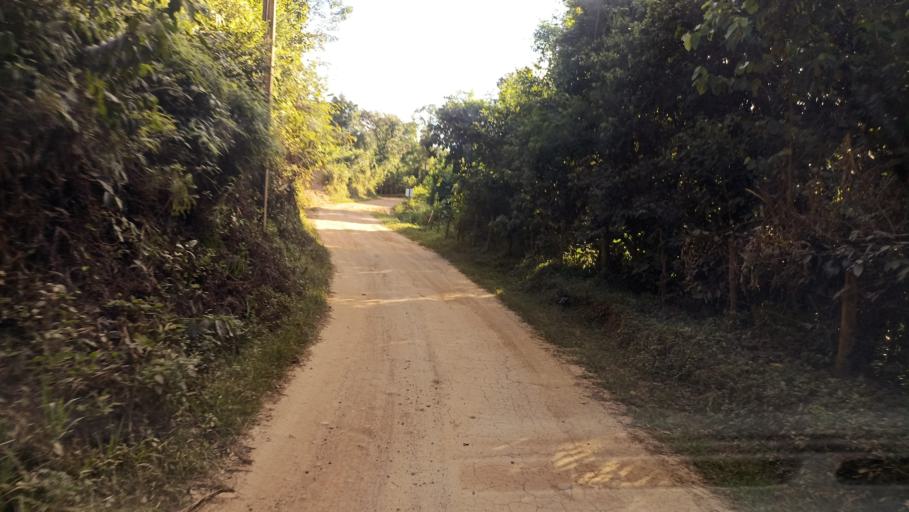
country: BR
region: Minas Gerais
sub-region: Ouro Preto
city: Ouro Preto
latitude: -20.3074
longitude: -43.5770
